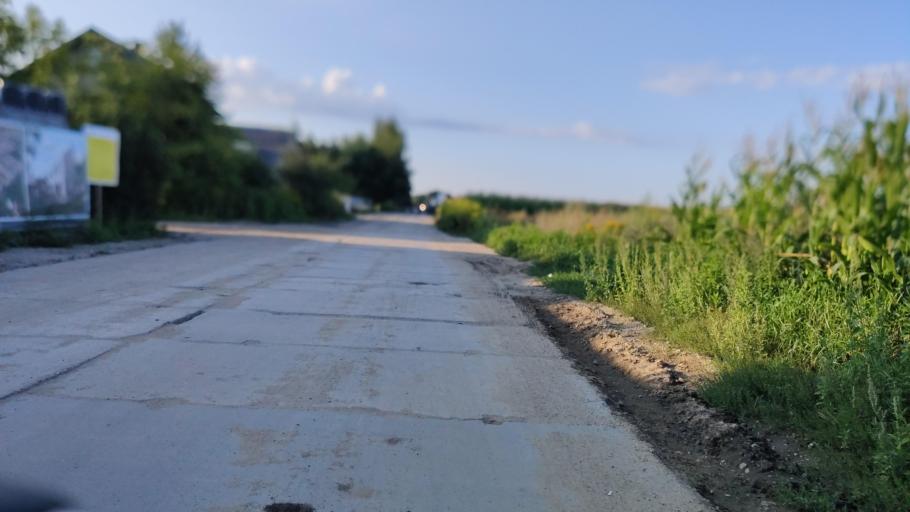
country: PL
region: Lower Silesian Voivodeship
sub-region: Powiat wroclawski
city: Zerniki Wroclawskie
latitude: 51.0489
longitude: 17.0656
